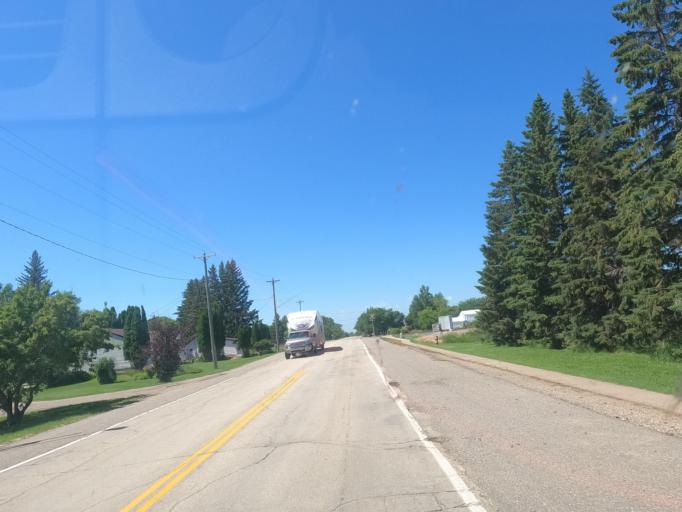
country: CA
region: Manitoba
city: Souris
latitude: 49.6209
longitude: -100.2649
